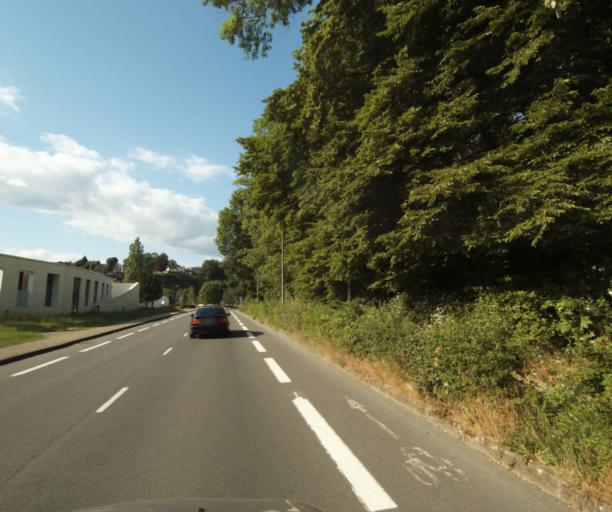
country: FR
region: Champagne-Ardenne
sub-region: Departement des Ardennes
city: Charleville-Mezieres
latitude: 49.7803
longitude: 4.7204
